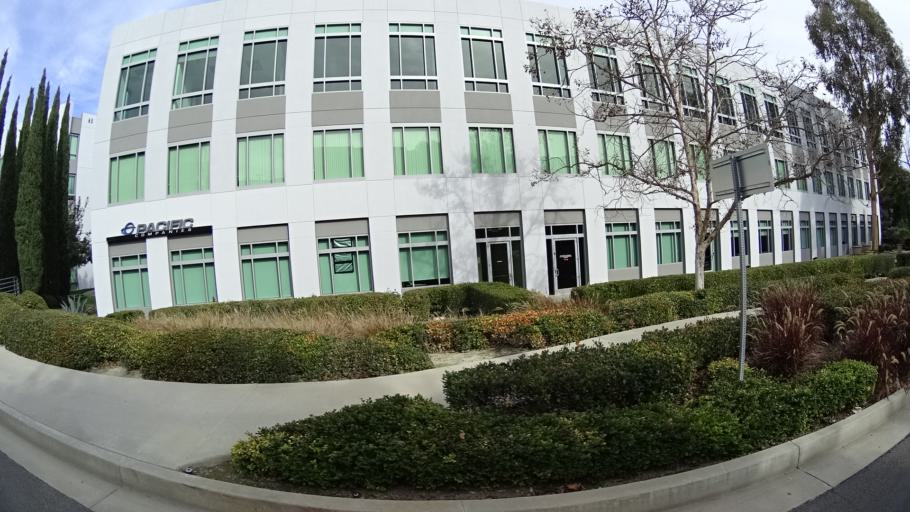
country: US
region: California
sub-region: Orange County
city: Aliso Viejo
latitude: 33.5819
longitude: -117.7276
